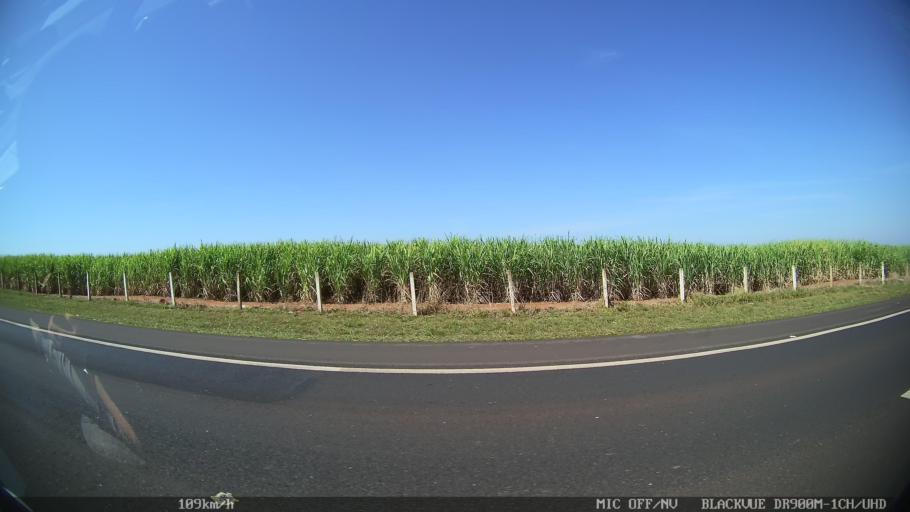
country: BR
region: Sao Paulo
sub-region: Batatais
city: Batatais
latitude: -20.8196
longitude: -47.5879
